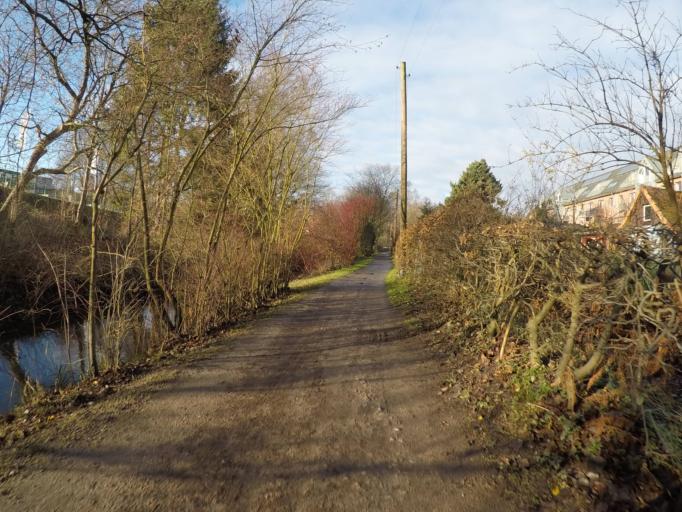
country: DE
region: Hamburg
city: Hamburg-Nord
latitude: 53.6049
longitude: 9.9684
